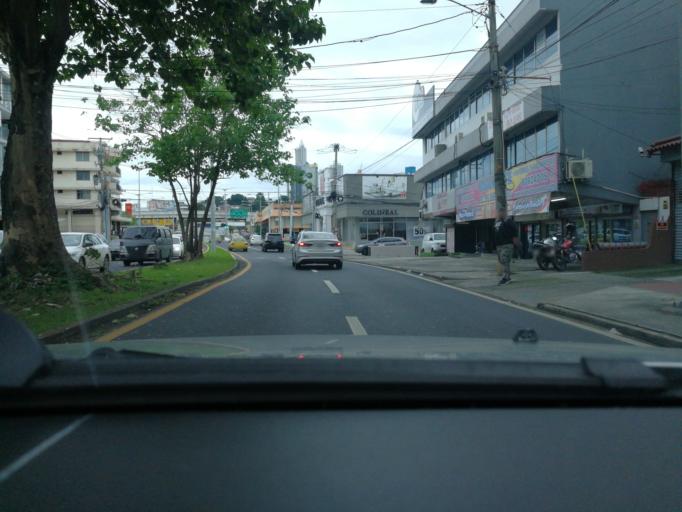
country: PA
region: Panama
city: Panama
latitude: 8.9947
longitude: -79.5260
